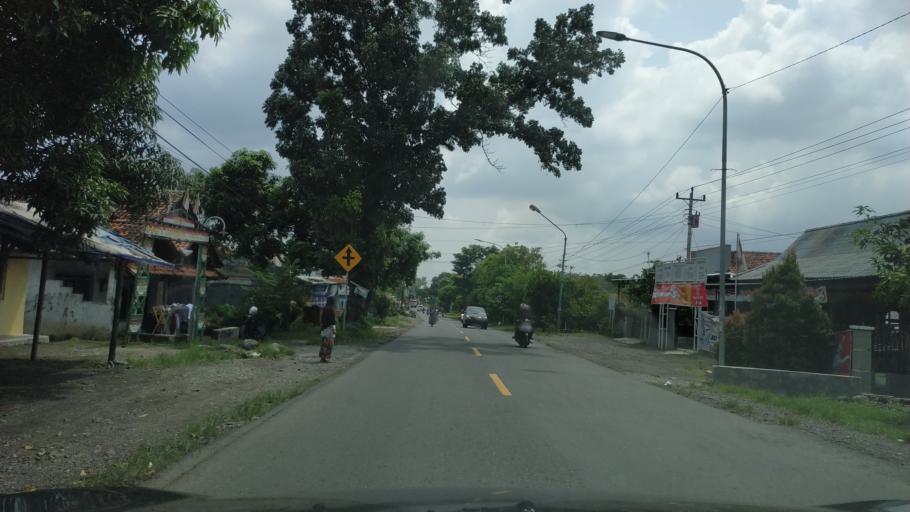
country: ID
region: Central Java
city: Lebaksiu
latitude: -7.0360
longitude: 109.1458
